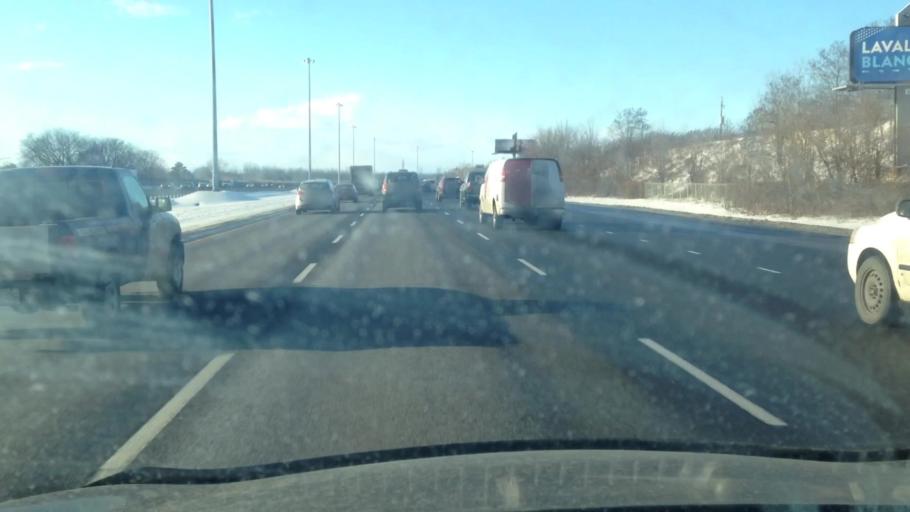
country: CA
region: Quebec
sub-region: Laurentides
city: Rosemere
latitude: 45.5887
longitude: -73.7932
